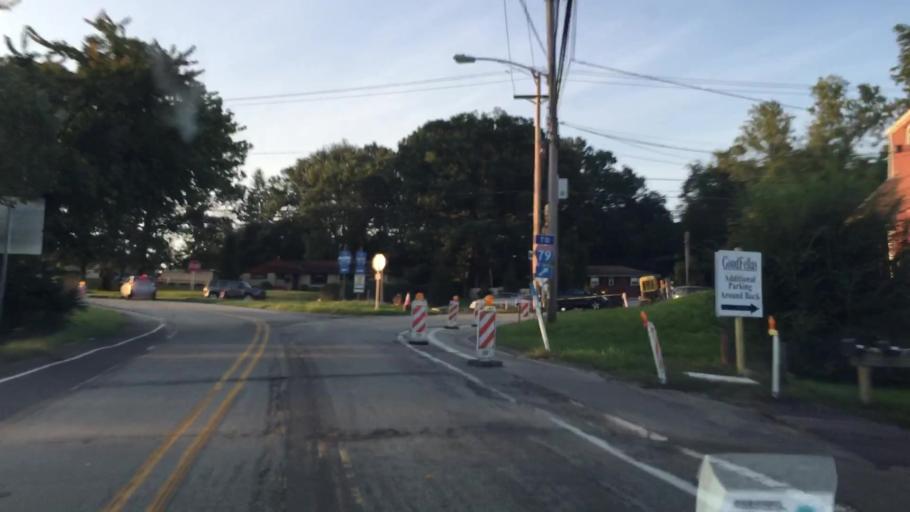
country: US
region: Pennsylvania
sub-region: Allegheny County
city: Franklin Park
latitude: 40.5535
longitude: -80.1059
